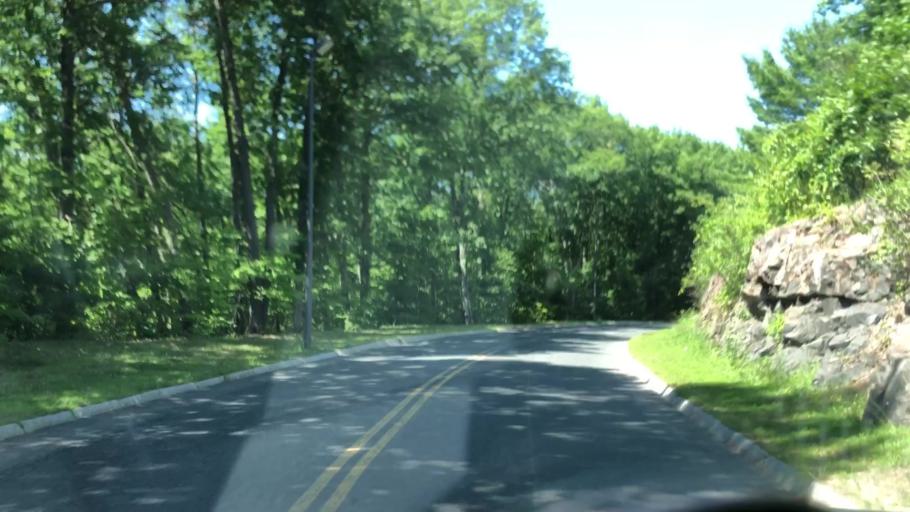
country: US
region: Massachusetts
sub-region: Hampden County
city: Holyoke
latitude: 42.1966
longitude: -72.6525
